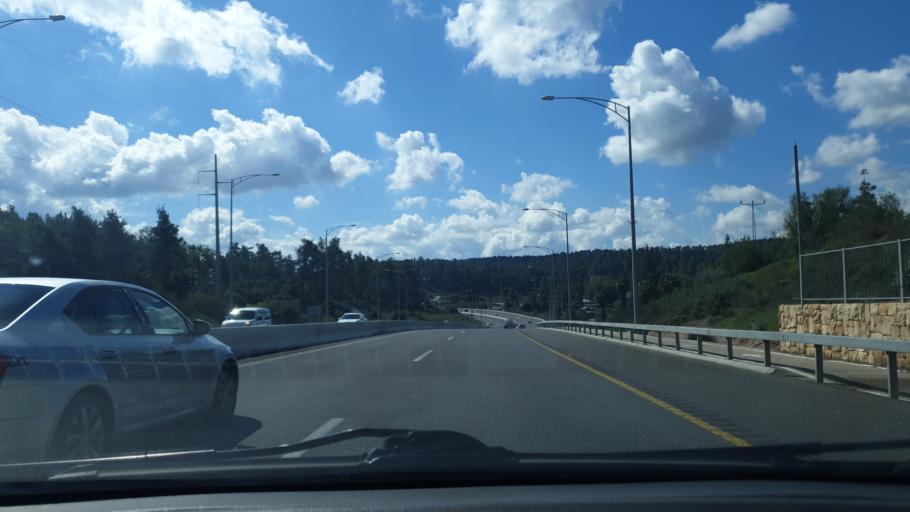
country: IL
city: Mevo horon
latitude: 31.8041
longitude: 35.0167
